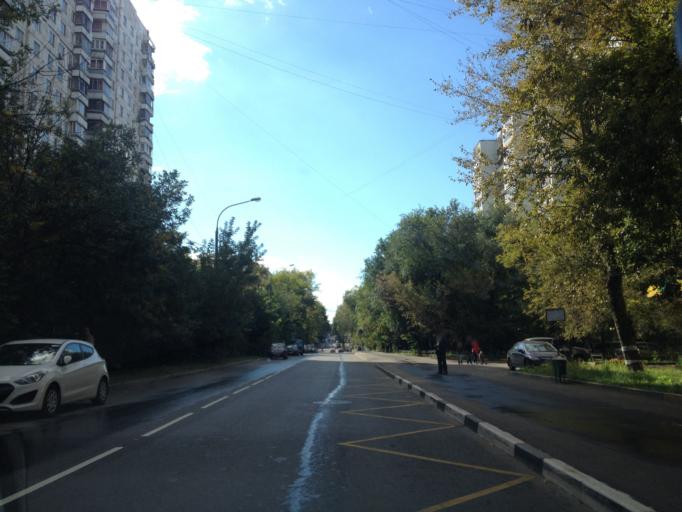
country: RU
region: Moscow
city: Metrogorodok
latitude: 55.7990
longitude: 37.7937
